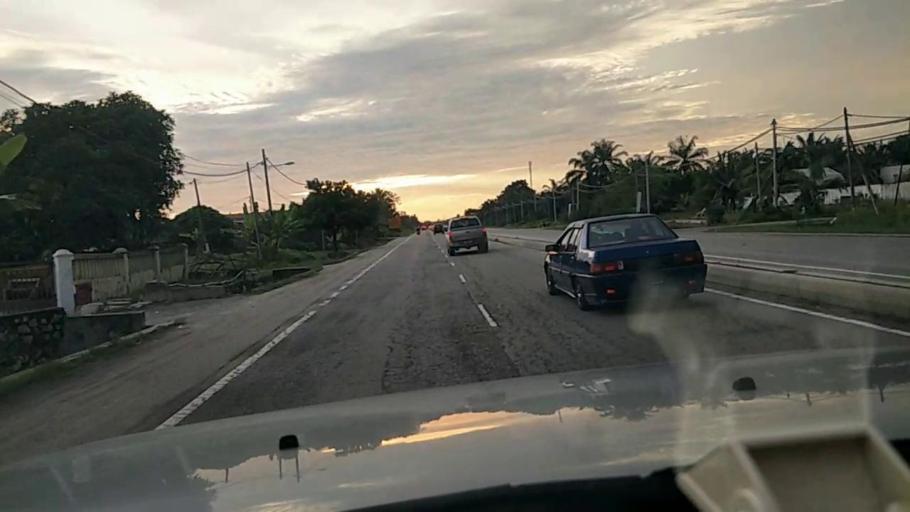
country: MY
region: Perak
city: Kampong Dungun
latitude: 3.1445
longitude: 101.3543
